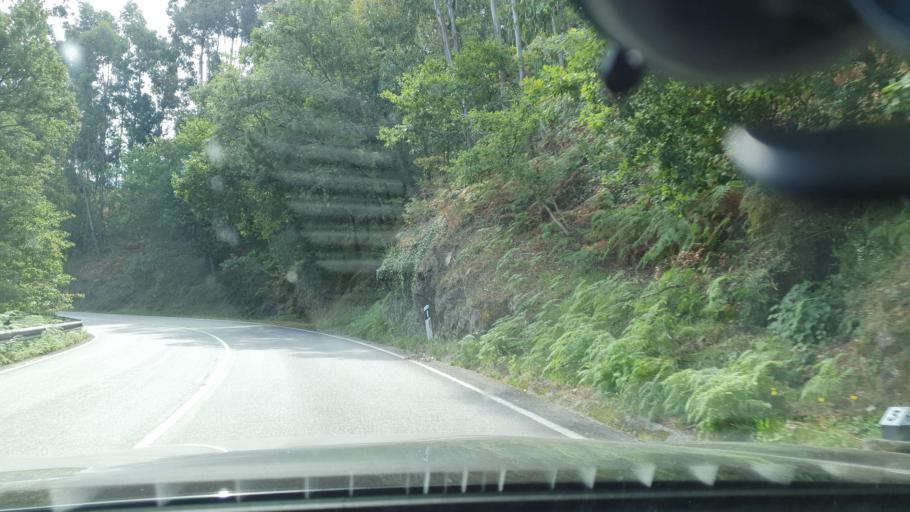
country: PT
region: Braga
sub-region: Vieira do Minho
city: Vieira do Minho
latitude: 41.6807
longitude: -8.1086
